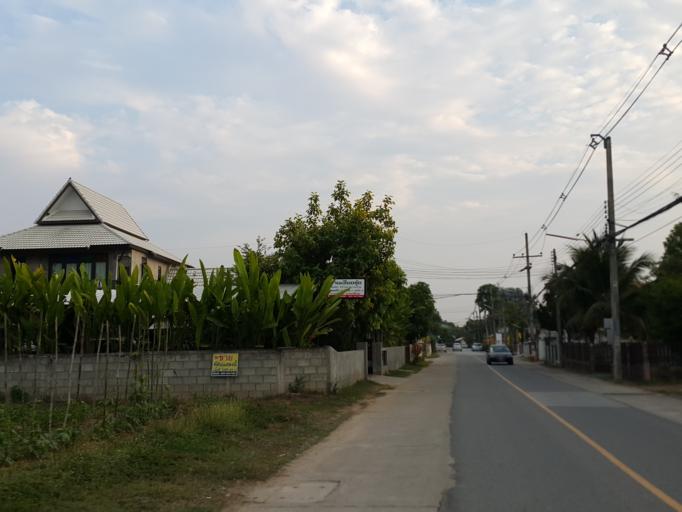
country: TH
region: Chiang Mai
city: San Sai
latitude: 18.8717
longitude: 99.1256
